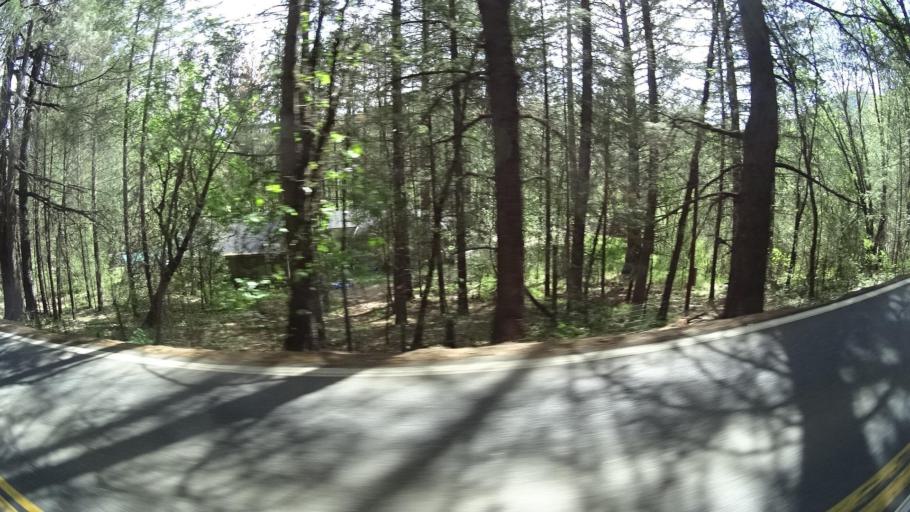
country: US
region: California
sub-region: Lake County
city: Cobb
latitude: 38.8851
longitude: -122.7278
